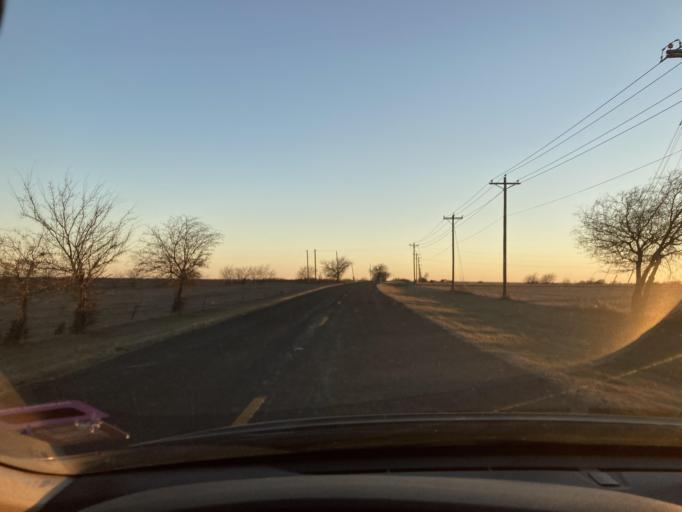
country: US
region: Texas
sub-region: Ellis County
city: Nash
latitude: 32.2959
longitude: -96.8919
